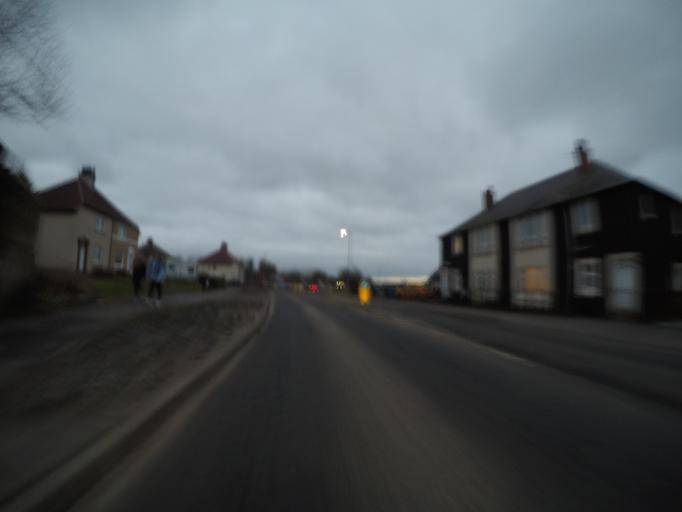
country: GB
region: Scotland
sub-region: North Ayrshire
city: Kilwinning
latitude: 55.6515
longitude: -4.6999
